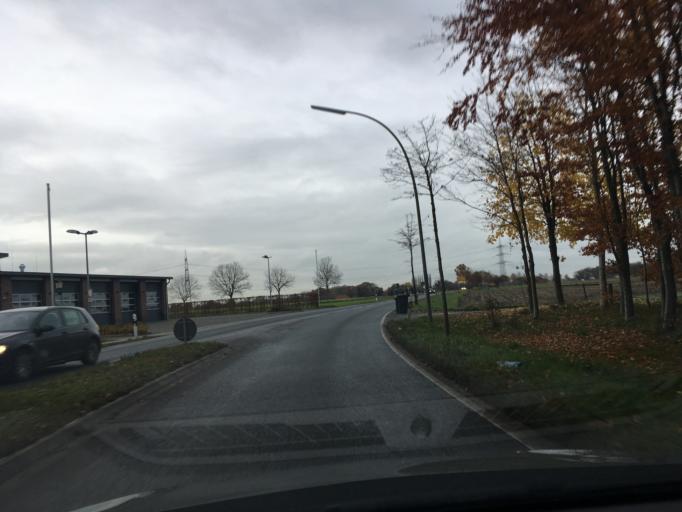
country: DE
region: North Rhine-Westphalia
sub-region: Regierungsbezirk Munster
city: Ahaus
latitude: 52.0935
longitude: 6.9700
